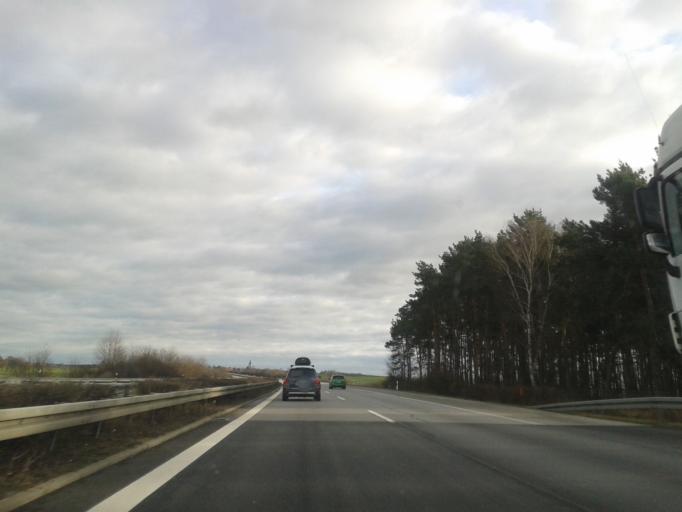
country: DE
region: Saxony
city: Guttau
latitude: 51.2084
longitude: 14.5902
